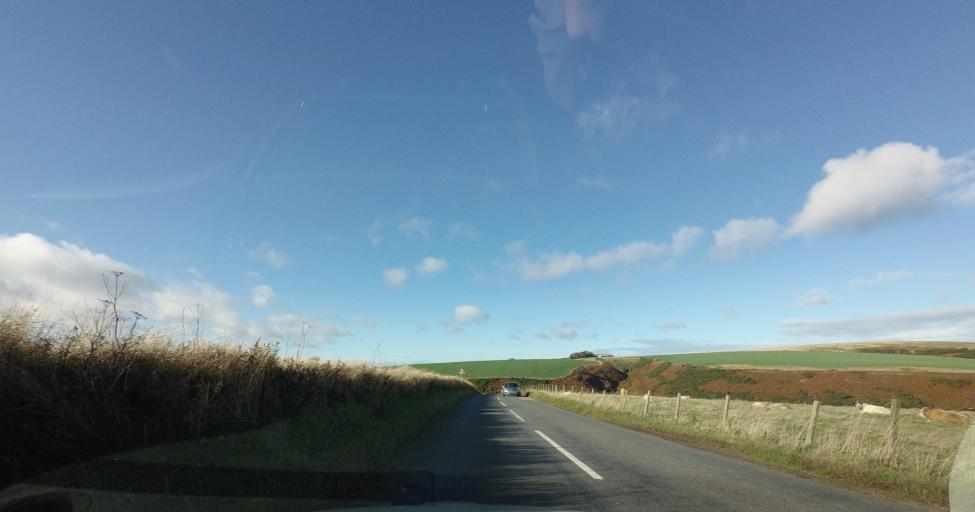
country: GB
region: Scotland
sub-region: Aberdeenshire
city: Macduff
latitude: 57.6615
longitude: -2.3522
